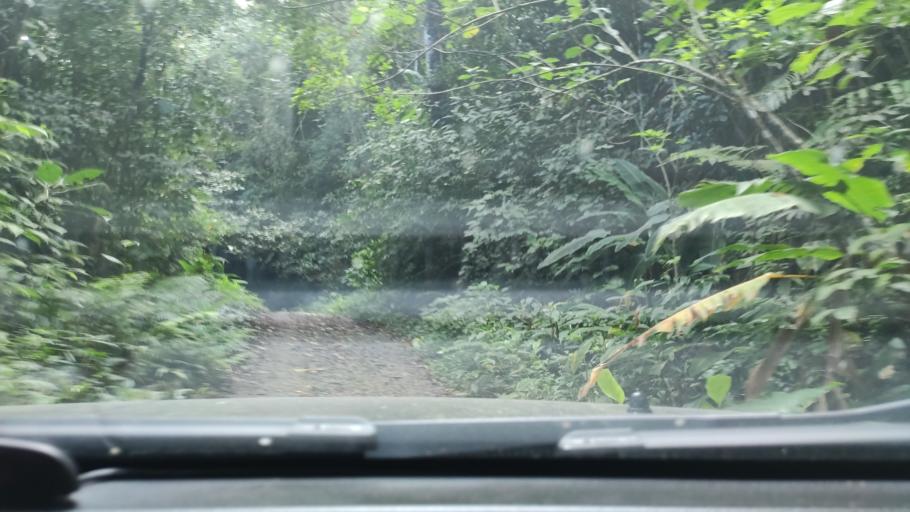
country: BR
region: Sao Paulo
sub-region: Sao Sebastiao
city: Sao Sebastiao
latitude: -23.7346
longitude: -45.4908
